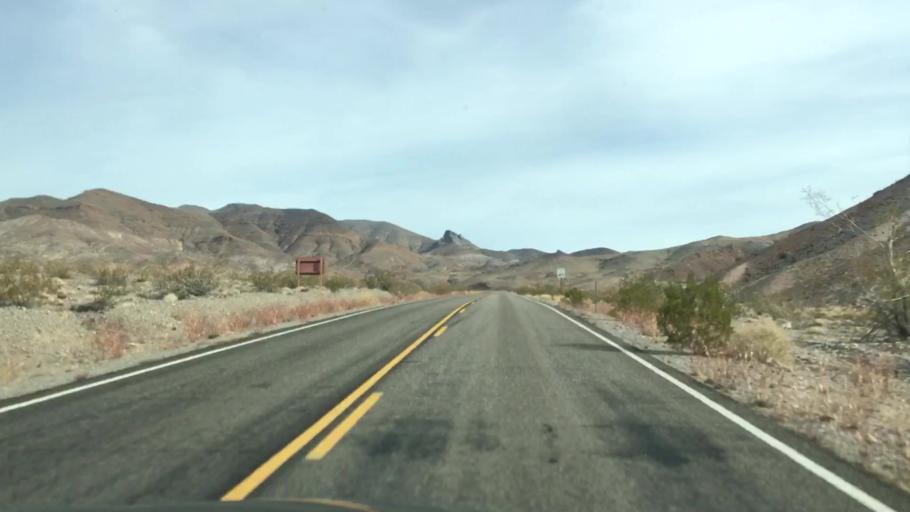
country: US
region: Nevada
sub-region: Nye County
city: Beatty
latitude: 36.7264
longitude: -116.9761
